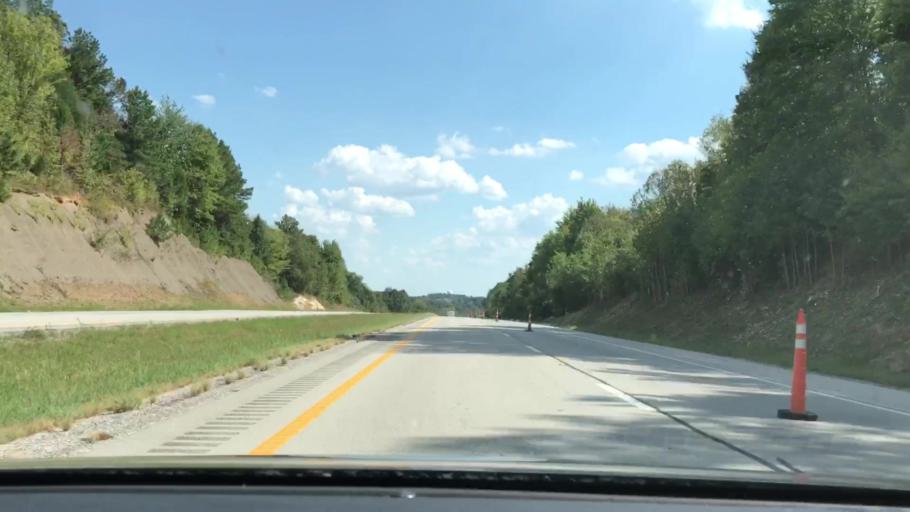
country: US
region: Kentucky
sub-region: Butler County
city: Morgantown
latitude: 37.2258
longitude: -86.7209
